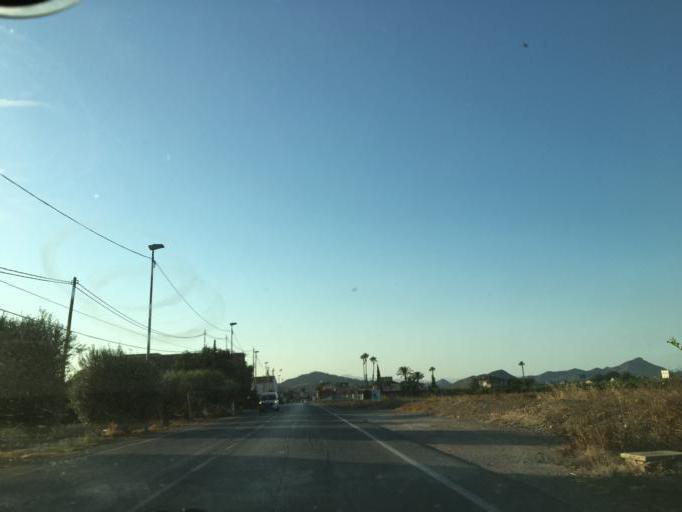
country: ES
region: Murcia
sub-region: Murcia
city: Murcia
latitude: 38.0033
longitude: -1.0774
